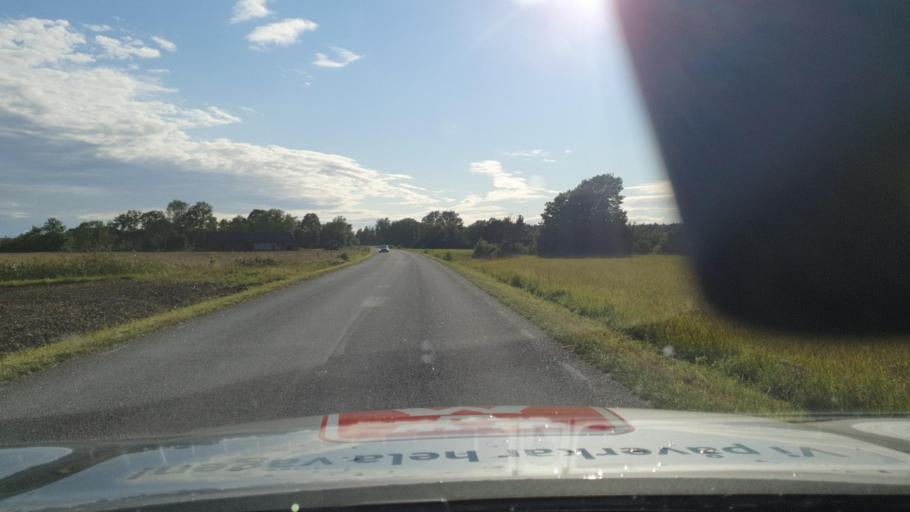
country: SE
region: Gotland
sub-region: Gotland
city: Visby
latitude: 57.5589
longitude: 18.5493
